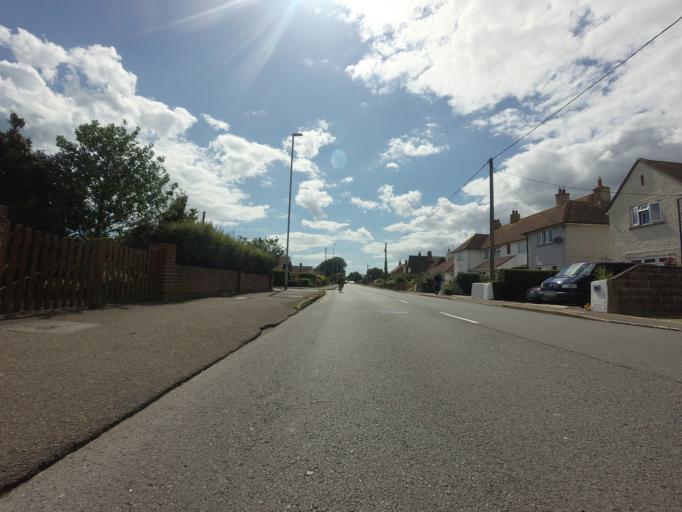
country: GB
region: England
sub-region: East Sussex
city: Pevensey
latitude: 50.8108
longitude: 0.3475
